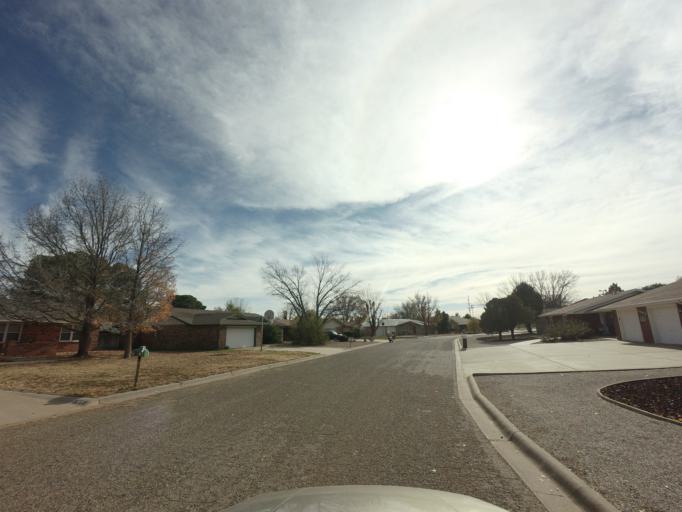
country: US
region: New Mexico
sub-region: Curry County
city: Clovis
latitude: 34.4131
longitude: -103.1836
